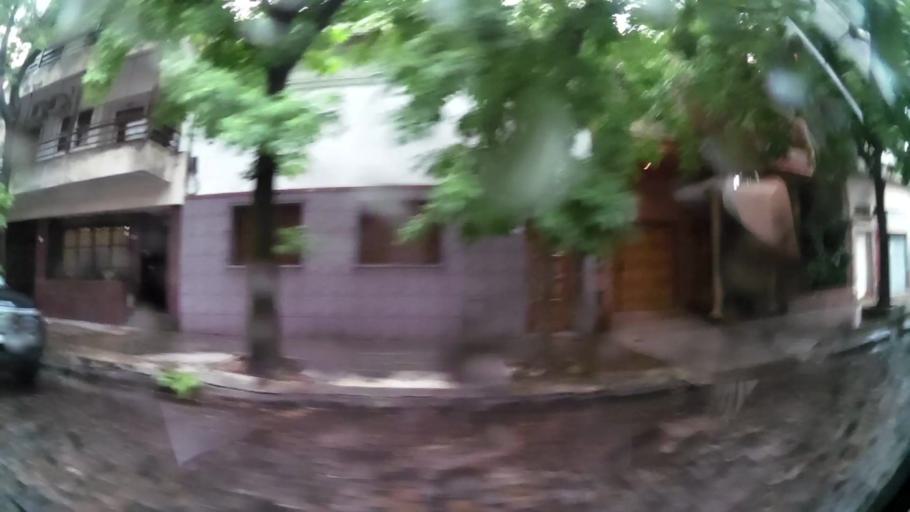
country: AR
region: Buenos Aires
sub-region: Partido de Avellaneda
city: Avellaneda
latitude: -34.6456
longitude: -58.3709
